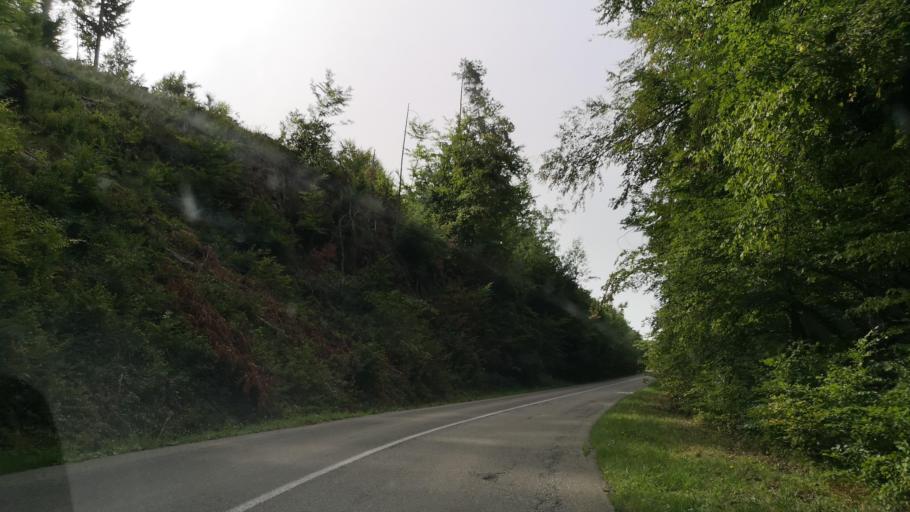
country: SK
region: Banskobystricky
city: Revuca
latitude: 48.5912
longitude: 20.0503
